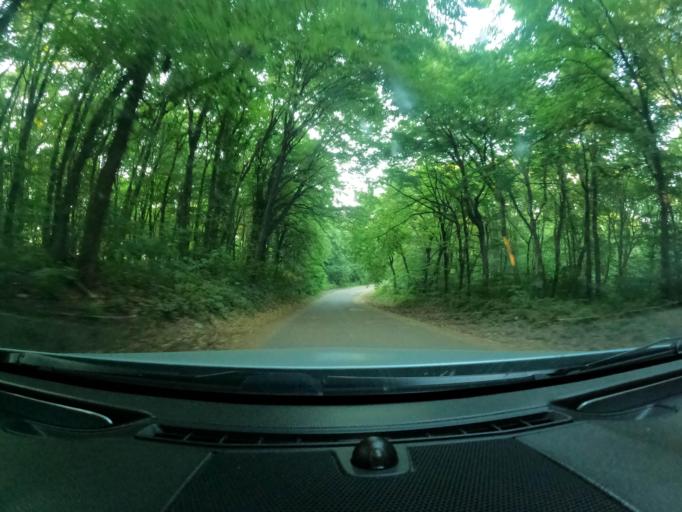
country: RS
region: Autonomna Pokrajina Vojvodina
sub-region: Juznobacki Okrug
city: Beocin
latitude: 45.1572
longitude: 19.7389
